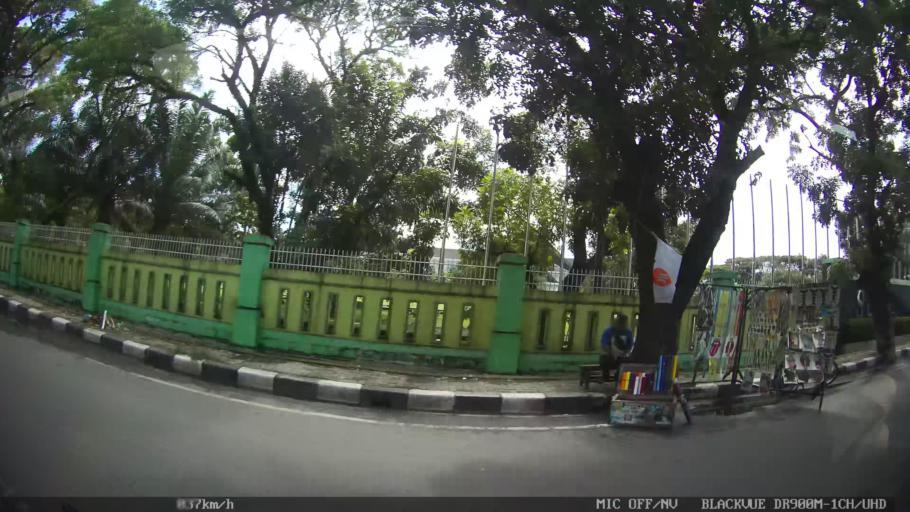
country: ID
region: North Sumatra
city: Medan
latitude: 3.6111
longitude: 98.7071
